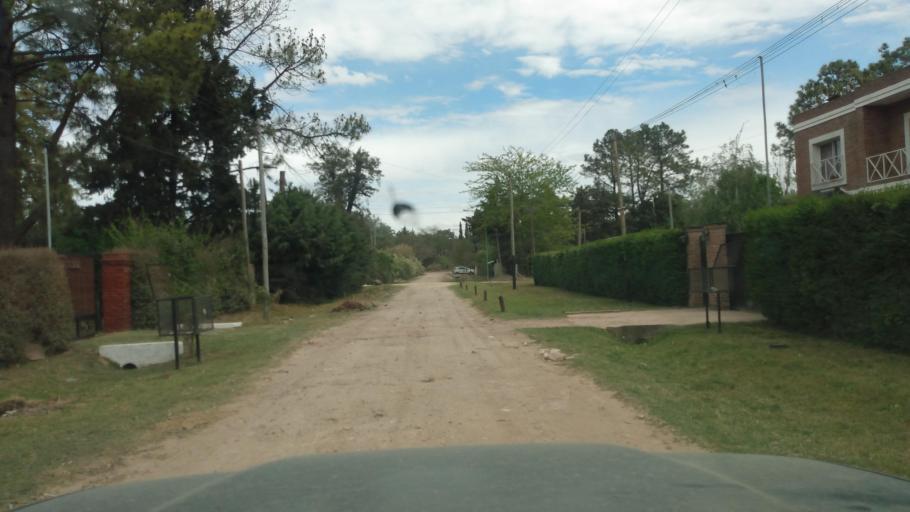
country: AR
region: Buenos Aires
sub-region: Partido de Lujan
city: Lujan
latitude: -34.5907
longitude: -59.1321
